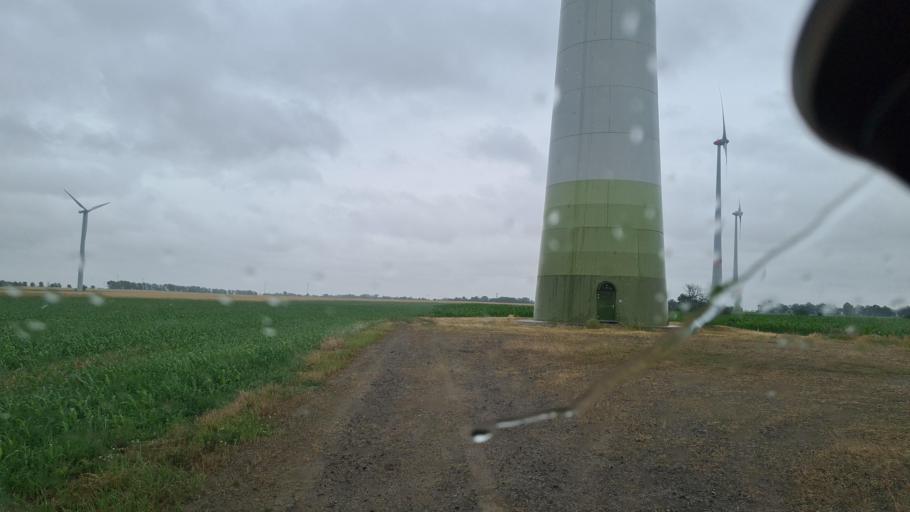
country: DE
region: Brandenburg
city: Juterbog
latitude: 51.9501
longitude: 13.1761
